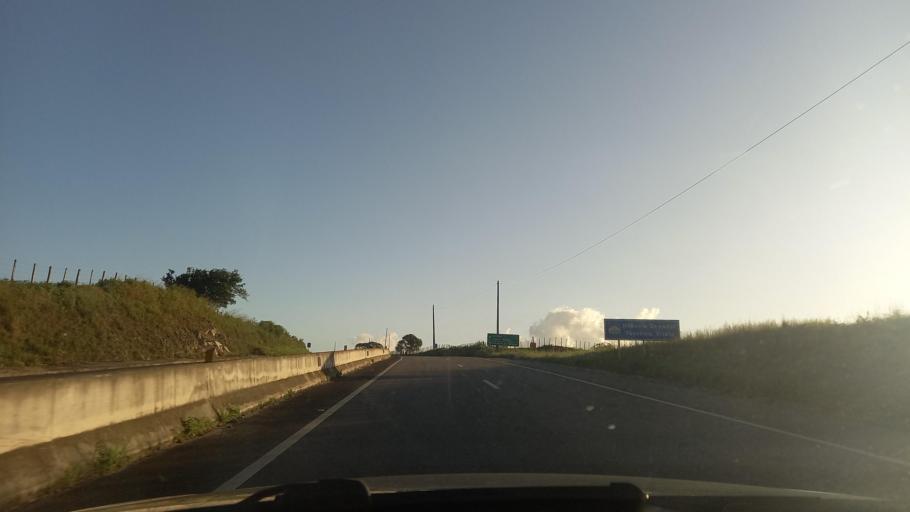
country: BR
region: Alagoas
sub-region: Limoeiro De Anadia
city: Limoeiro de Anadia
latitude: -9.7423
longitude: -36.4984
